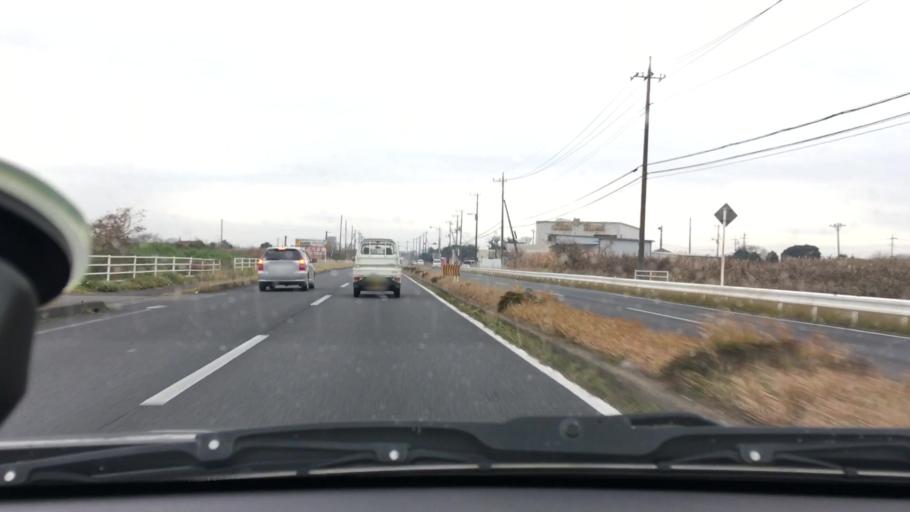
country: JP
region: Ibaraki
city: Kashima-shi
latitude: 35.9137
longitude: 140.6202
